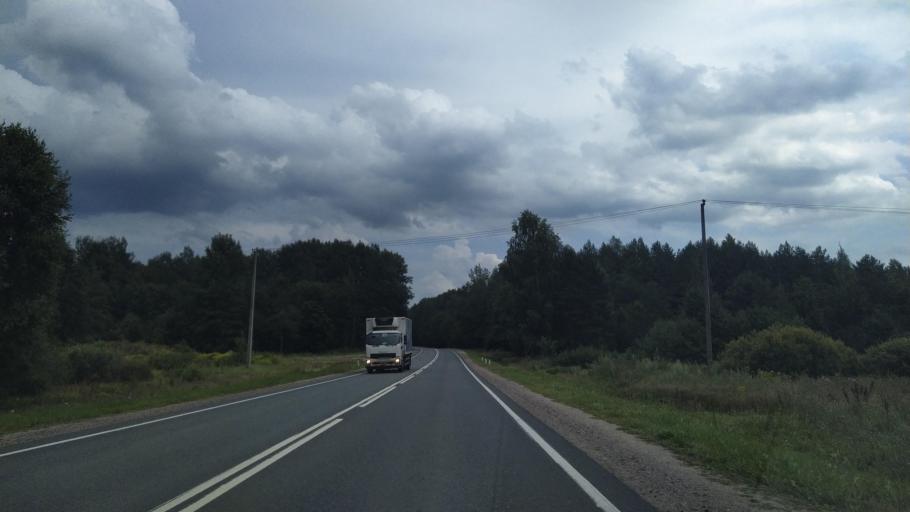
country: RU
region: Pskov
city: Pskov
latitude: 57.8321
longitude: 28.5341
